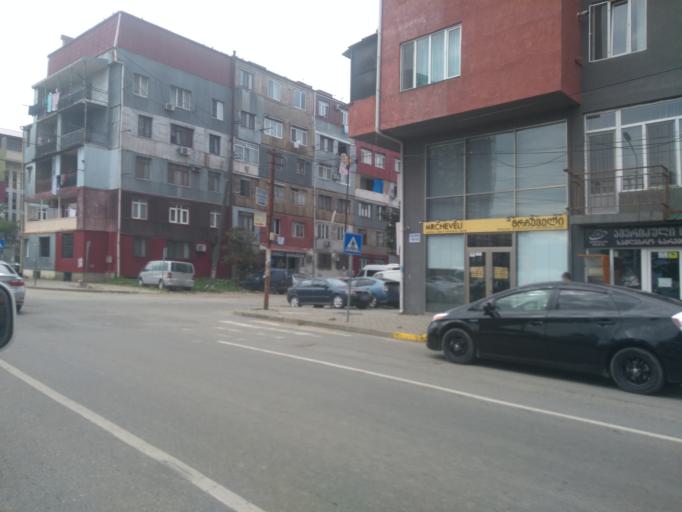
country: GE
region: Ajaria
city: Batumi
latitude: 41.6344
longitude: 41.6245
